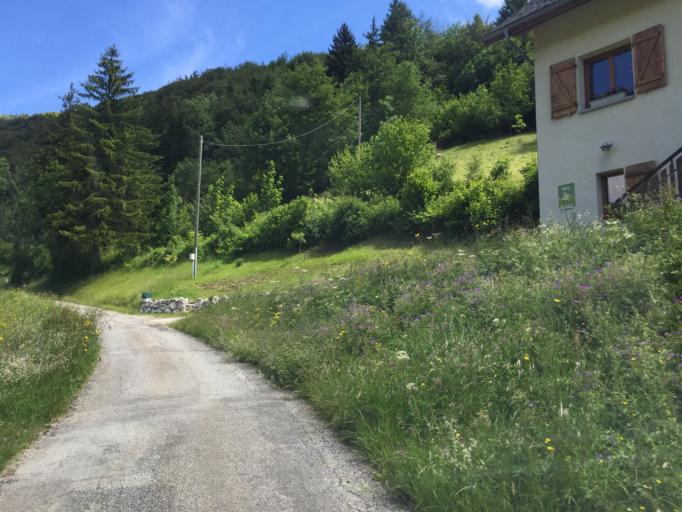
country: FR
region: Rhone-Alpes
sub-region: Departement de la Savoie
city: Vimines
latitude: 45.4766
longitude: 5.8920
